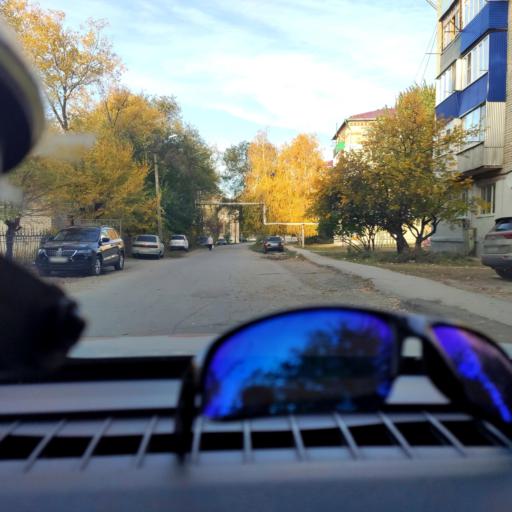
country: RU
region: Samara
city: Chapayevsk
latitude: 52.9951
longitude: 49.7804
